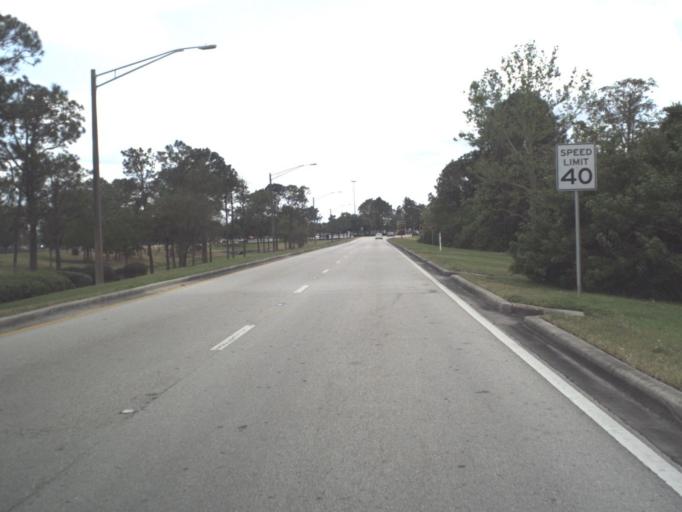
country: US
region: Florida
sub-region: Orange County
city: Taft
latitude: 28.4214
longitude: -81.3346
